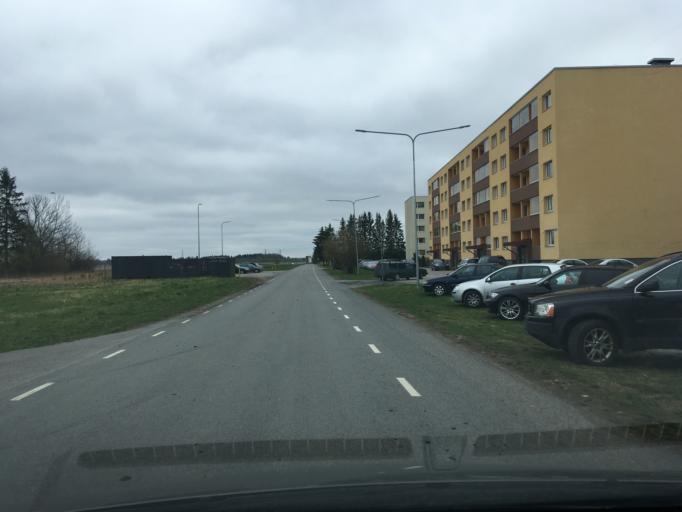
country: EE
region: Harju
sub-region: Rae vald
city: Vaida
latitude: 59.2885
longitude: 24.9798
